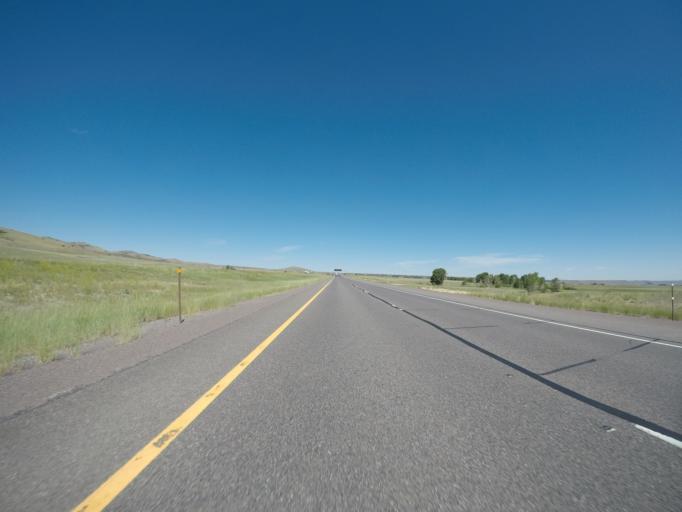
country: US
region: Wyoming
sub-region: Albany County
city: Laramie
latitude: 41.5855
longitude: -106.1748
